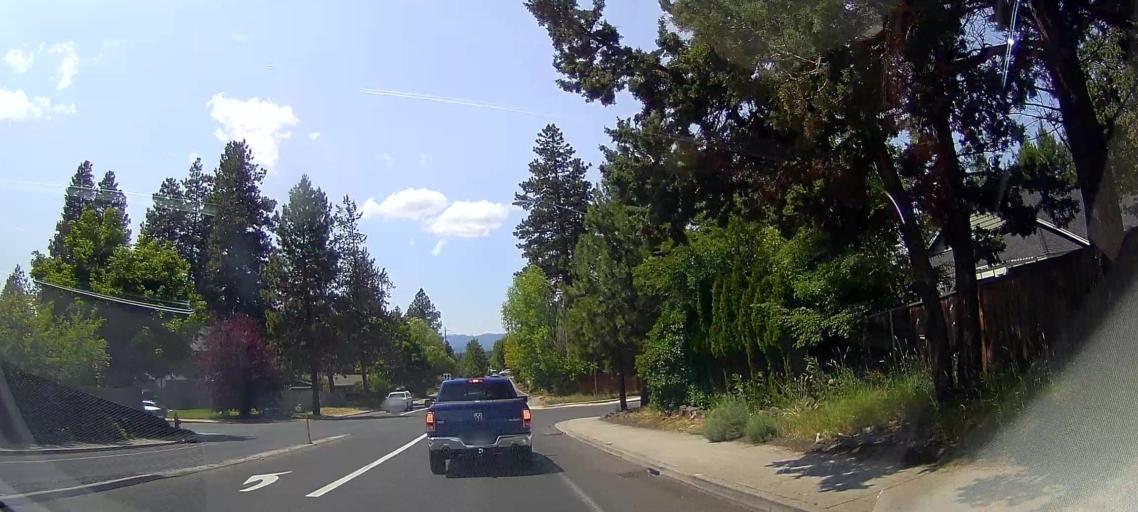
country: US
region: Oregon
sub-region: Deschutes County
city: Bend
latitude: 44.0394
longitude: -121.3114
